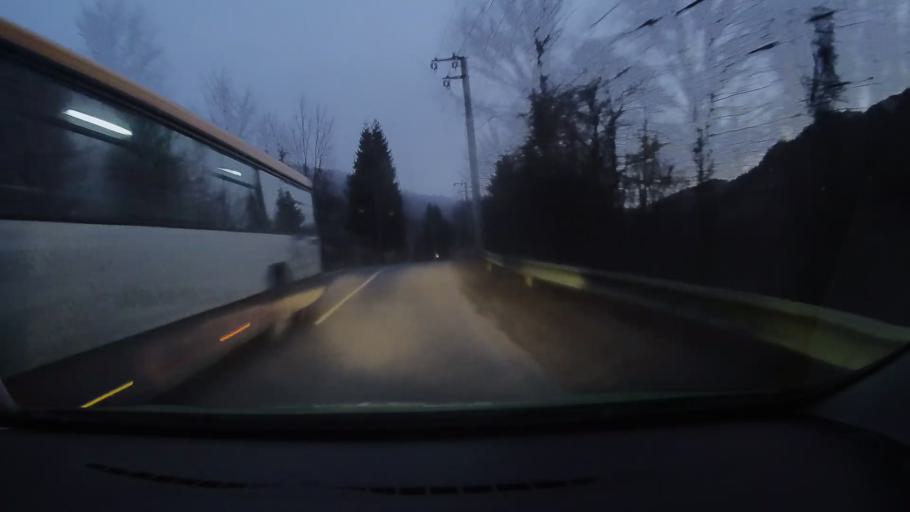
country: RO
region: Prahova
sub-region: Comuna Valea Doftanei
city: Tesila
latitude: 45.2806
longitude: 25.7269
